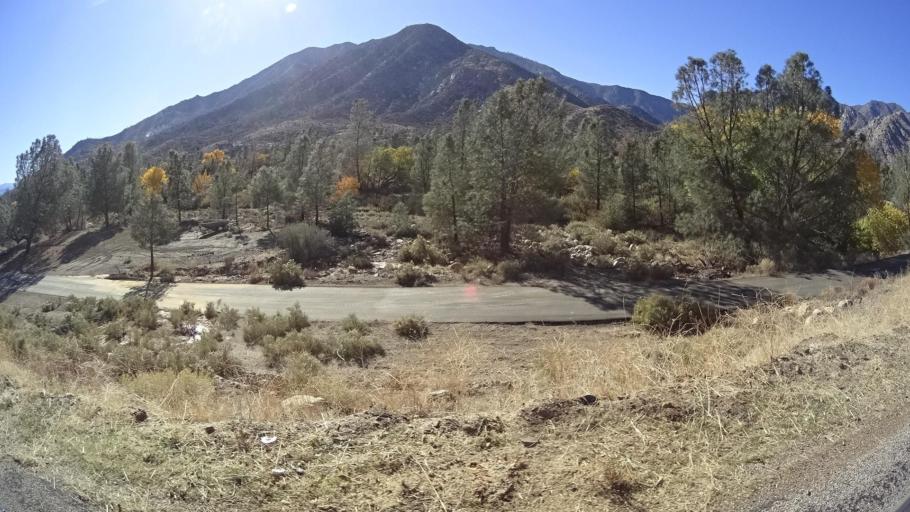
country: US
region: California
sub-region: Kern County
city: Kernville
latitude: 35.7784
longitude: -118.4374
